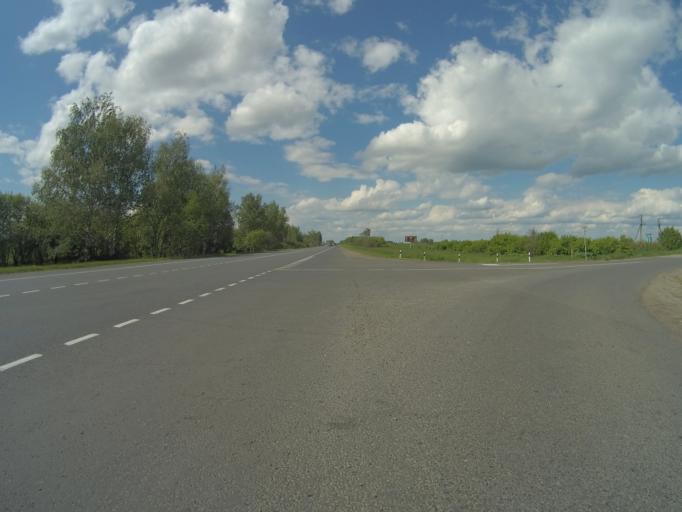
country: RU
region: Vladimir
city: Suzdal'
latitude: 56.3492
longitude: 40.4737
